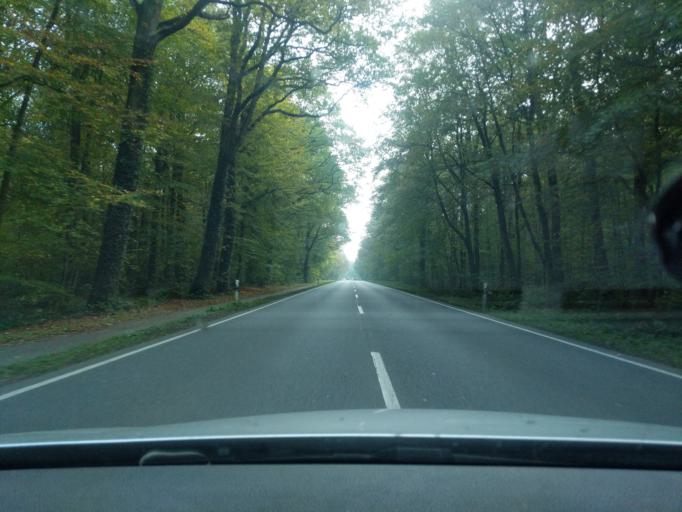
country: DE
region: Lower Saxony
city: Himmelpforten
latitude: 53.6038
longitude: 9.3196
